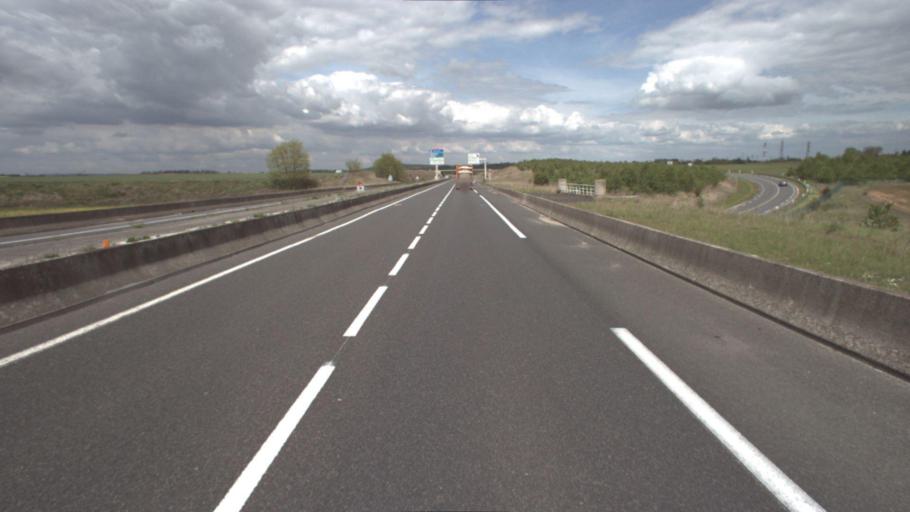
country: FR
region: Ile-de-France
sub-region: Departement de Seine-et-Marne
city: Villenoy
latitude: 48.9348
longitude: 2.8464
